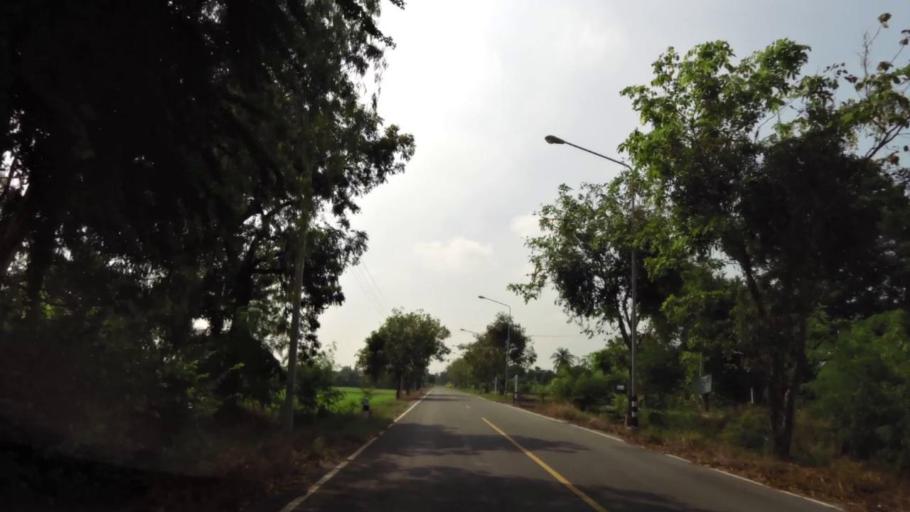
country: TH
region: Ang Thong
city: Pho Thong
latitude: 14.6116
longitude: 100.3961
